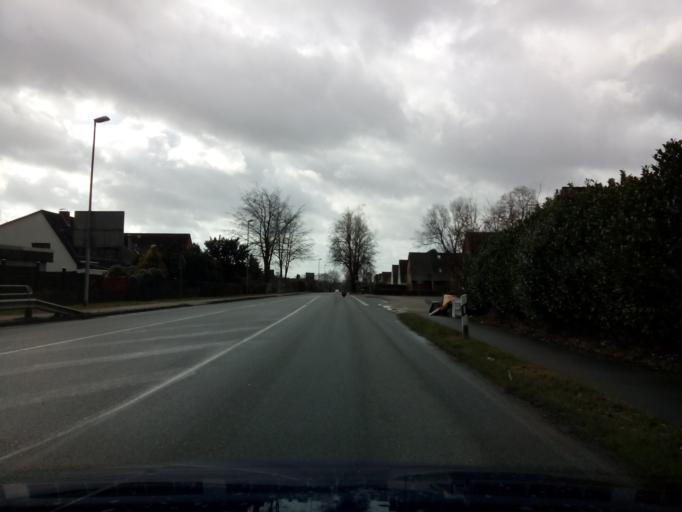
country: DE
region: Lower Saxony
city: Ritterhude
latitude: 53.1946
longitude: 8.7518
